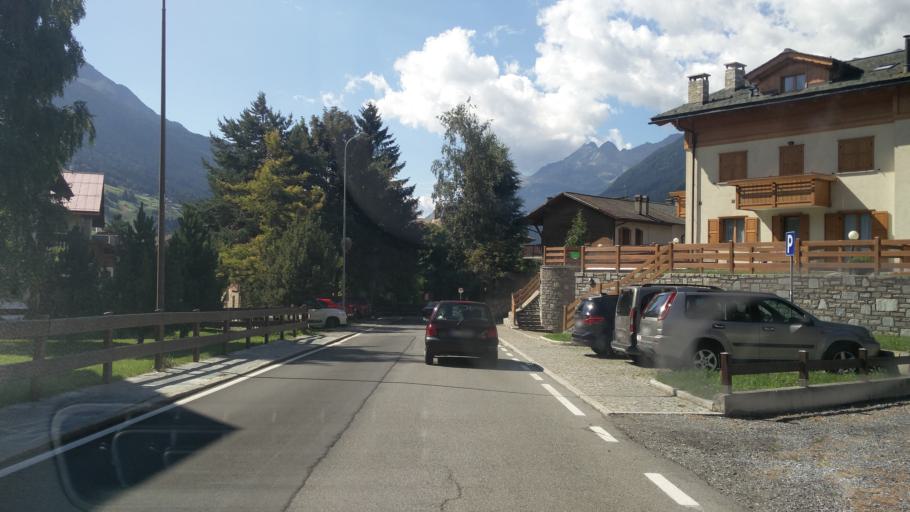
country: IT
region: Lombardy
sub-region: Provincia di Sondrio
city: Bormio
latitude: 46.4670
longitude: 10.3669
